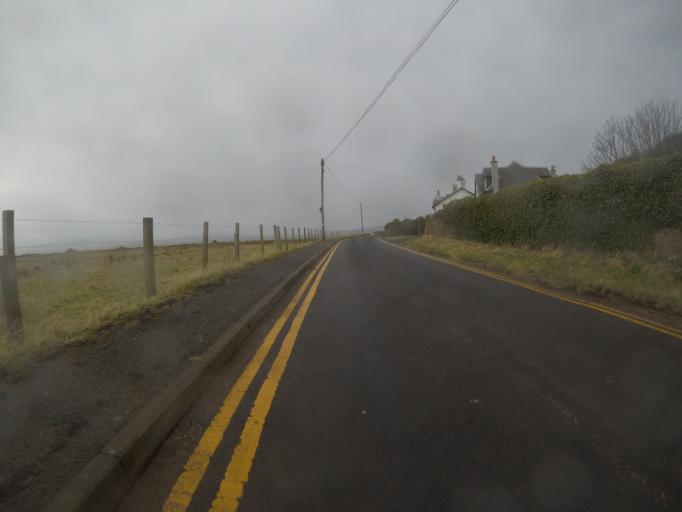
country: GB
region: Scotland
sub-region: North Ayrshire
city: West Kilbride
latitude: 55.6973
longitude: -4.9005
